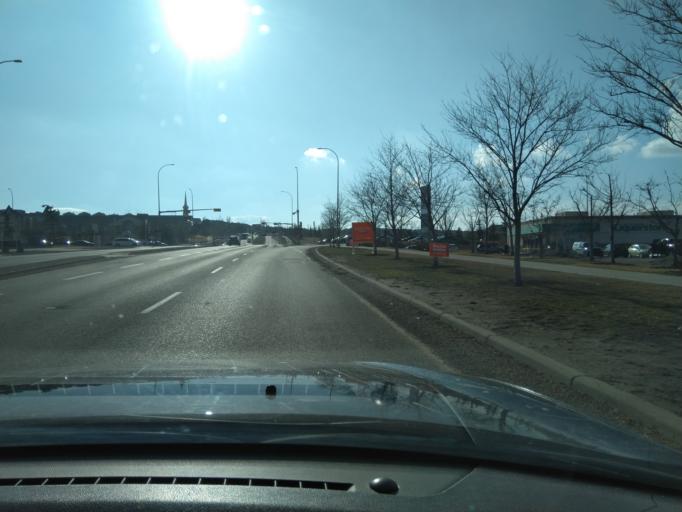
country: CA
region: Alberta
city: Calgary
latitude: 51.1604
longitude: -114.0691
